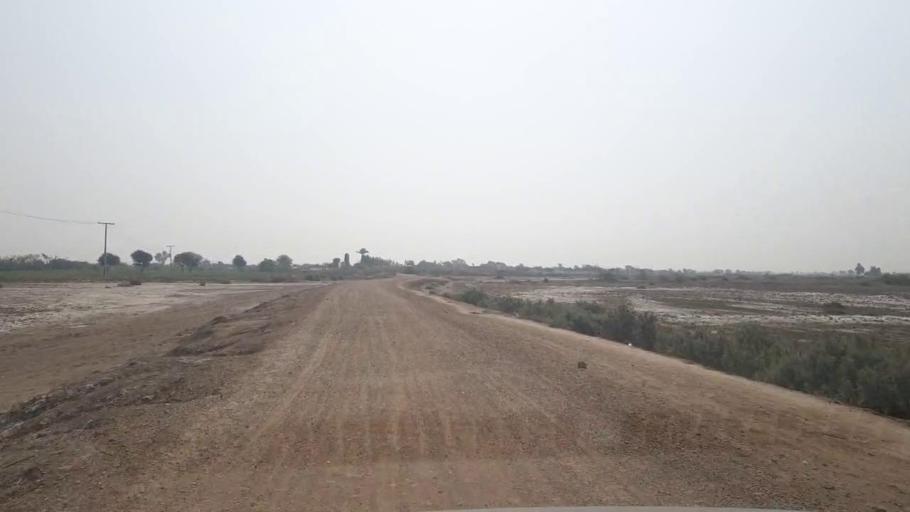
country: PK
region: Sindh
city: Umarkot
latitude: 25.4300
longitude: 69.6515
